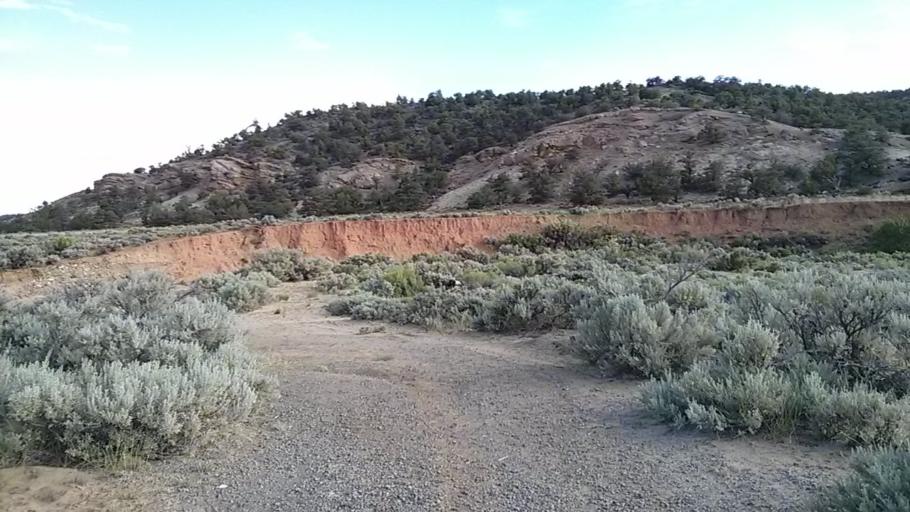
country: US
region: Utah
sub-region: Wayne County
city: Loa
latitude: 37.8618
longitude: -111.6368
